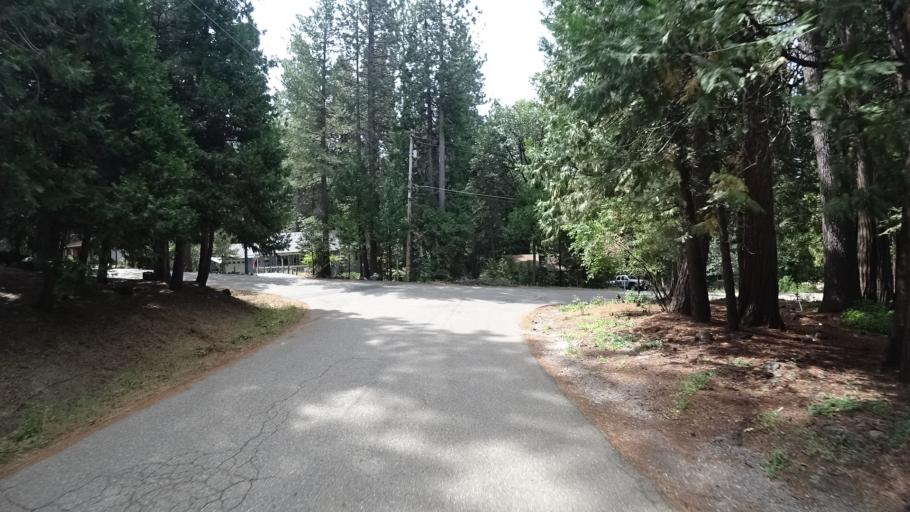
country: US
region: California
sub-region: Calaveras County
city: Arnold
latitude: 38.2432
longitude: -120.3557
